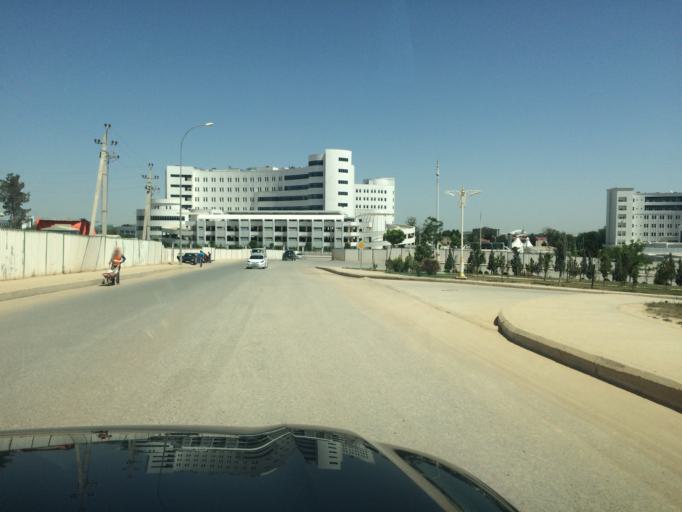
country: TM
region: Ahal
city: Ashgabat
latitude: 37.9383
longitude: 58.3622
